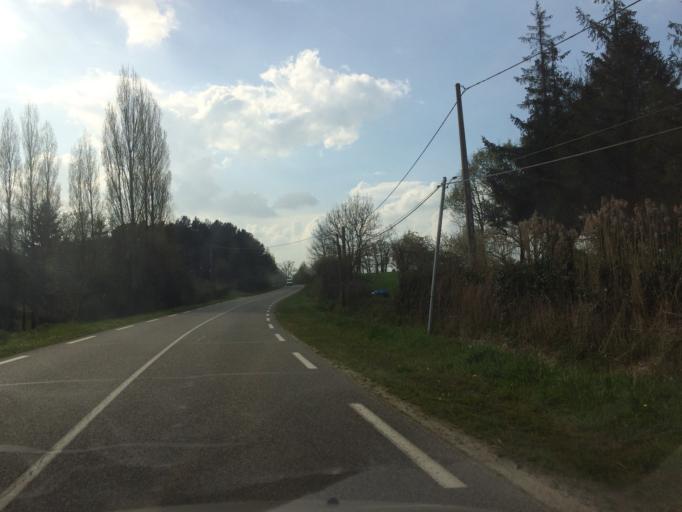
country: FR
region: Pays de la Loire
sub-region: Departement de la Loire-Atlantique
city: Blain
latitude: 47.4826
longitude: -1.7993
